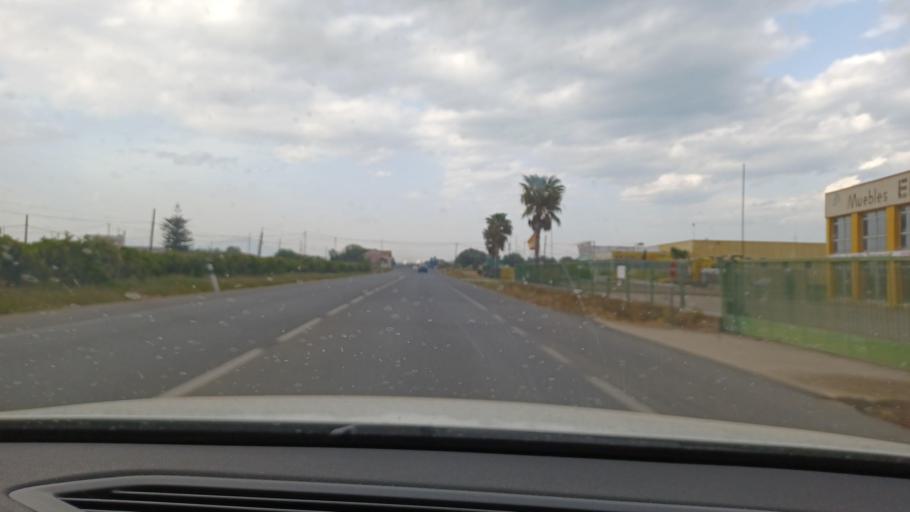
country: ES
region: Valencia
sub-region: Provincia de Castello
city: Benicarlo
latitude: 40.4402
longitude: 0.4424
